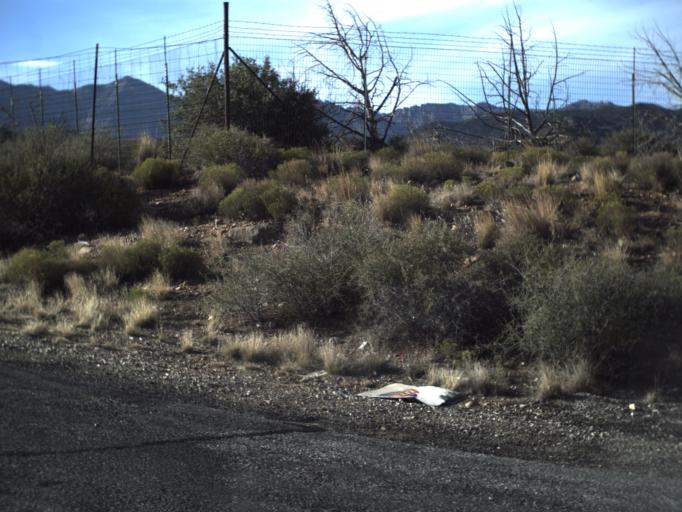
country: US
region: Utah
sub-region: Washington County
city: Toquerville
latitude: 37.3265
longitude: -113.2860
